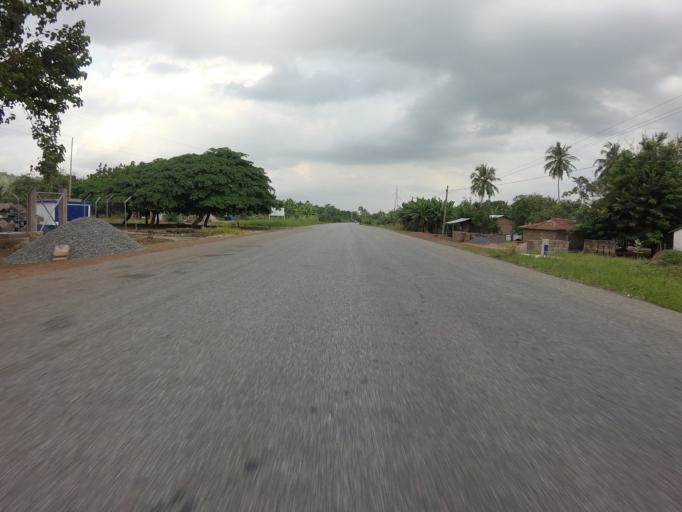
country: GH
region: Volta
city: Ho
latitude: 6.4829
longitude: 0.4935
